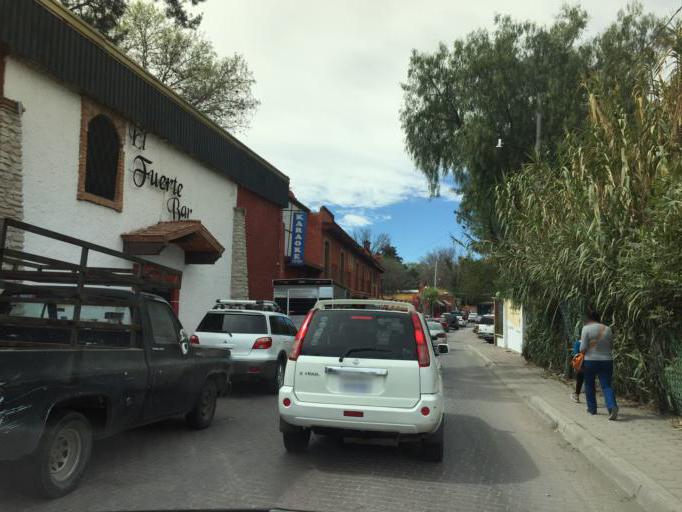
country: MX
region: Queretaro
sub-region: Tequisquiapan
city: Tequisquiapan
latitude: 20.5246
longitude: -99.8893
